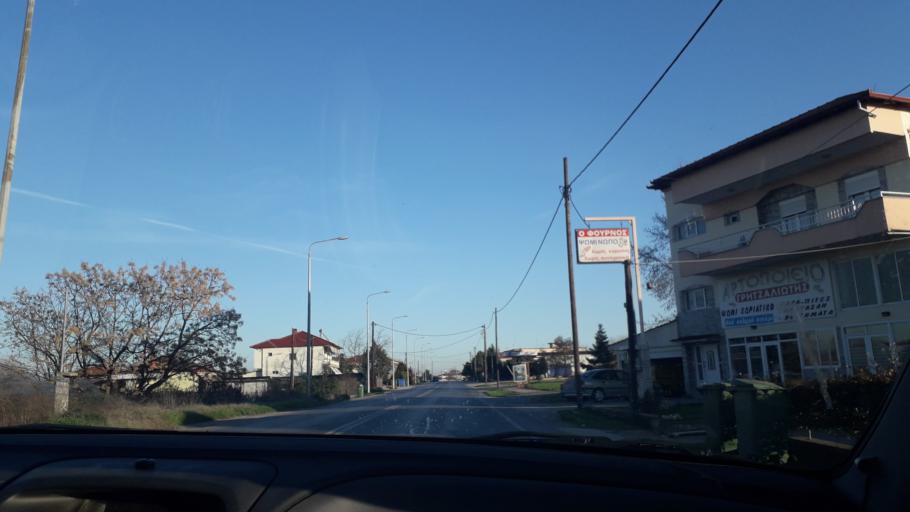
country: GR
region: Central Macedonia
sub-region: Nomos Imathias
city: Alexandreia
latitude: 40.5976
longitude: 22.4587
